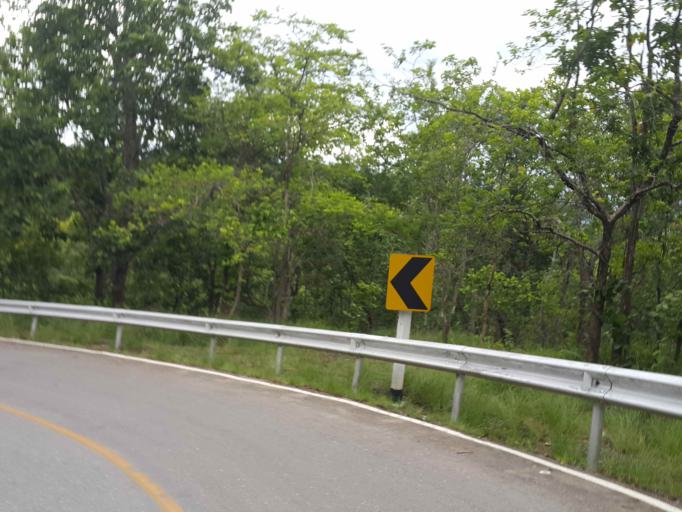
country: TH
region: Chiang Mai
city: Mae Chaem
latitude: 18.5141
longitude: 98.4235
